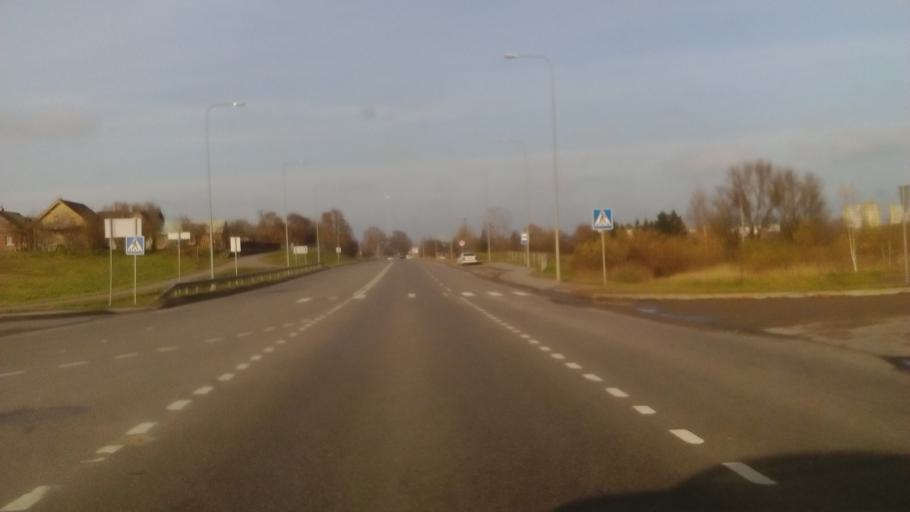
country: LT
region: Alytaus apskritis
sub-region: Alytus
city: Alytus
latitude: 54.4048
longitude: 24.0028
